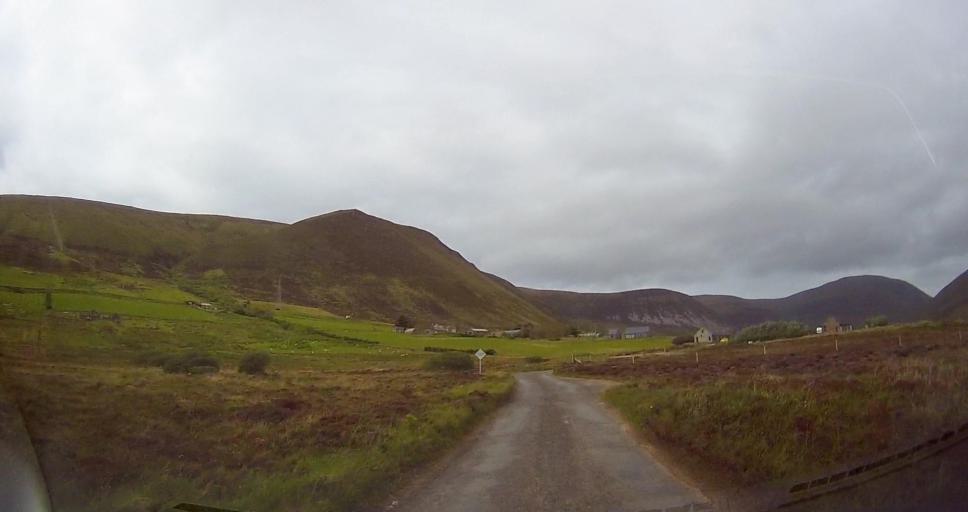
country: GB
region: Scotland
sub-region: Orkney Islands
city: Stromness
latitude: 58.8743
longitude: -3.3865
